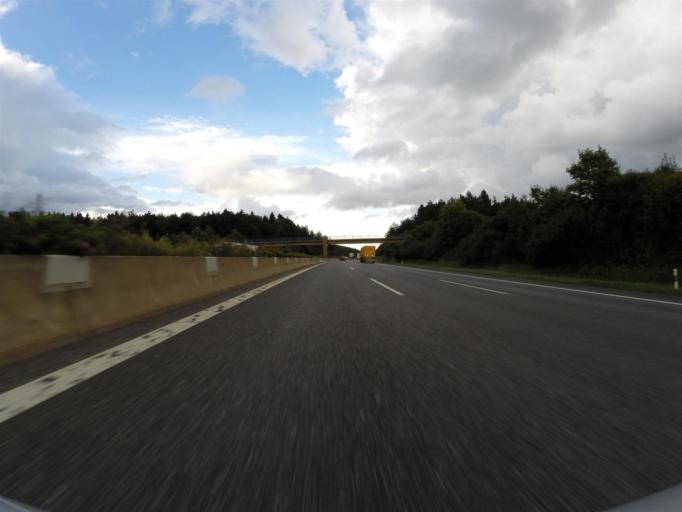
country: DE
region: Bavaria
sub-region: Regierungsbezirk Mittelfranken
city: Simmelsdorf
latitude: 49.6120
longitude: 11.3761
